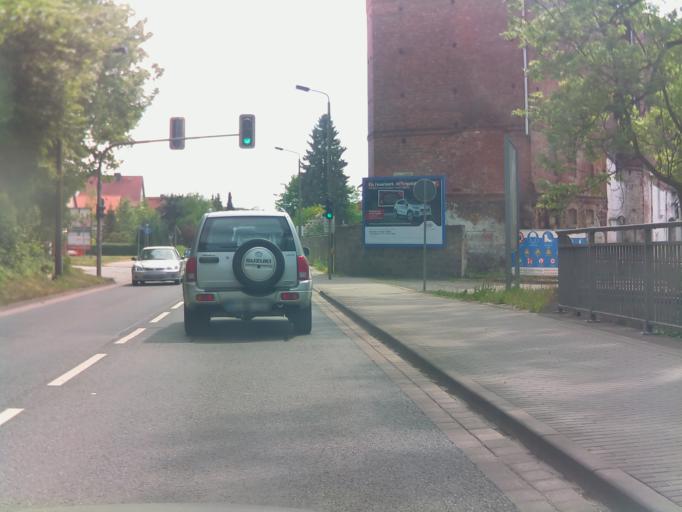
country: DE
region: Thuringia
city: Nordhausen
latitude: 51.5272
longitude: 10.7825
